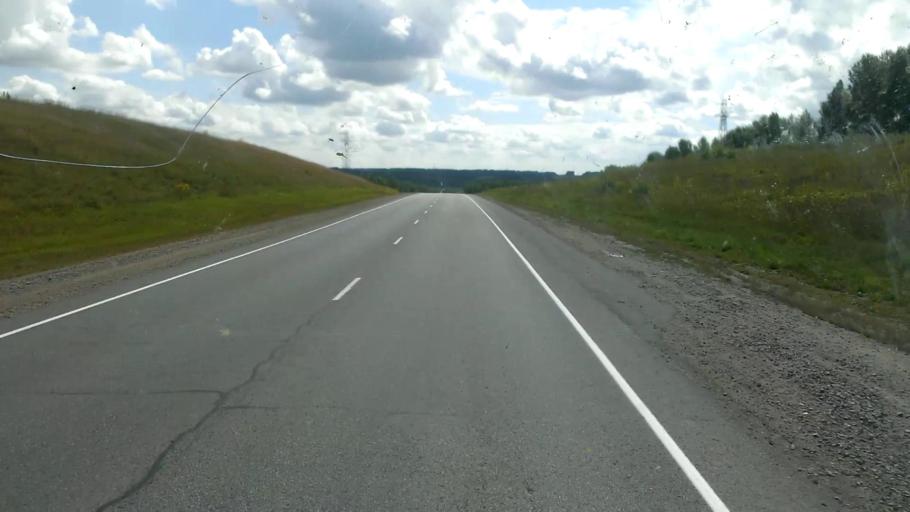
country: RU
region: Altai Krai
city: Troitskoye
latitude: 52.9452
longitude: 84.7740
